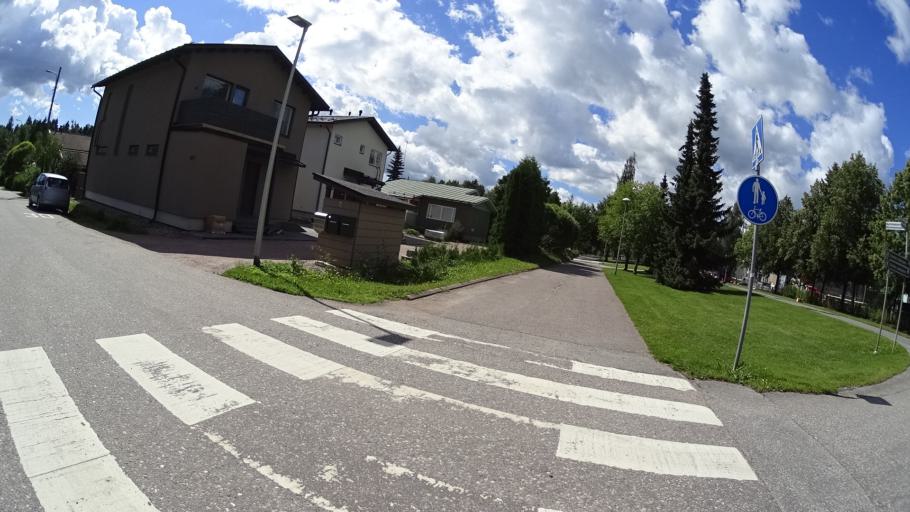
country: FI
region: Uusimaa
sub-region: Helsinki
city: Teekkarikylae
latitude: 60.2759
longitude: 24.8475
